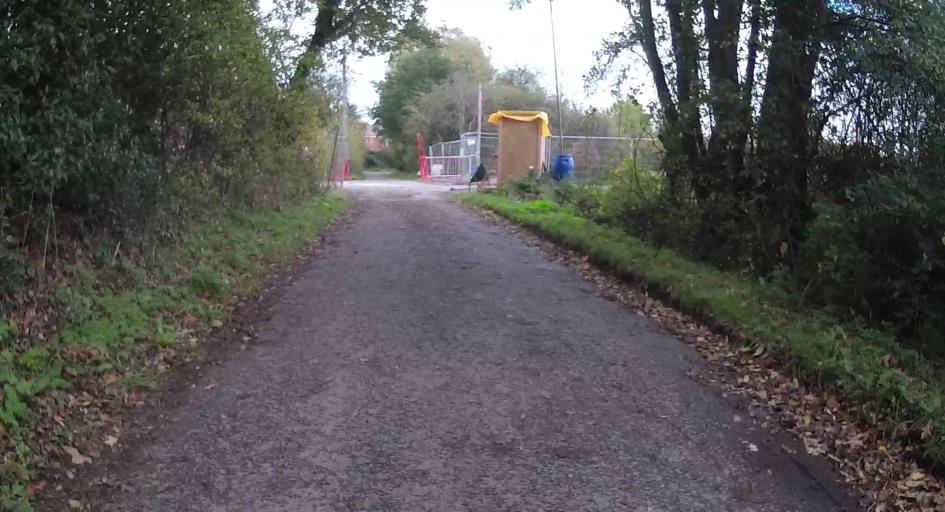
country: GB
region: England
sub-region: Wokingham
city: Swallowfield
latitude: 51.3982
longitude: -0.9654
